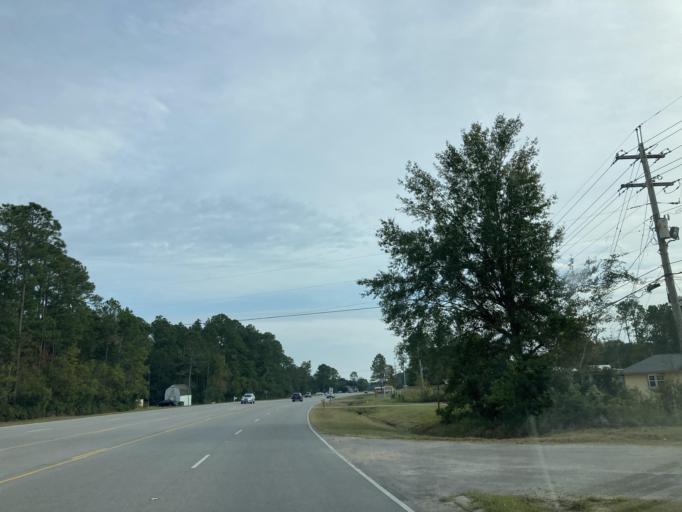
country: US
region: Mississippi
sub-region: Jackson County
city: Saint Martin
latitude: 30.4791
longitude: -88.8507
